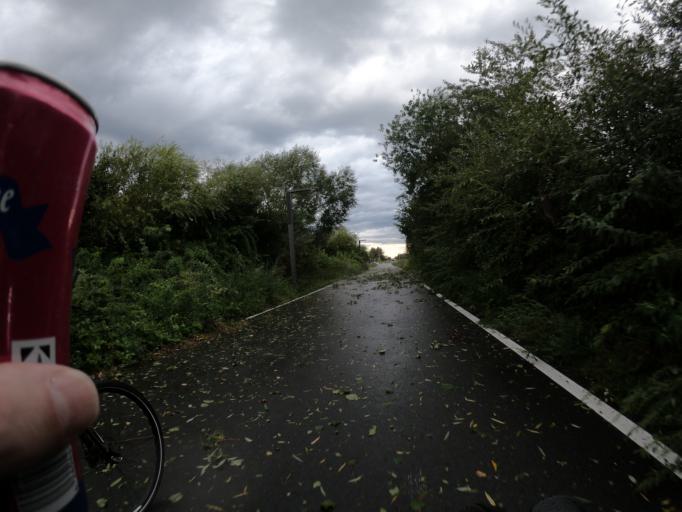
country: DE
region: Hesse
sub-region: Regierungsbezirk Darmstadt
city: Erzhausen
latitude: 49.9620
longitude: 8.6545
